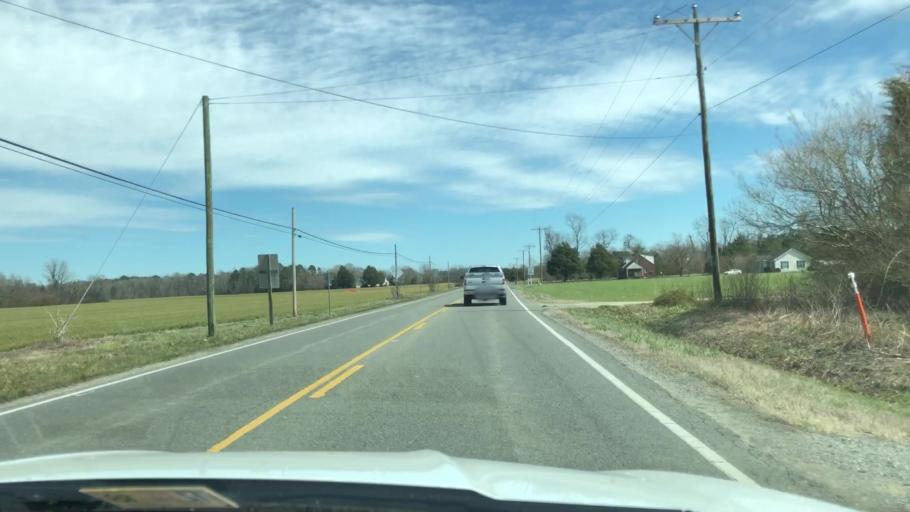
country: US
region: Virginia
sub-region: Lancaster County
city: Lancaster
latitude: 37.7681
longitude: -76.4460
